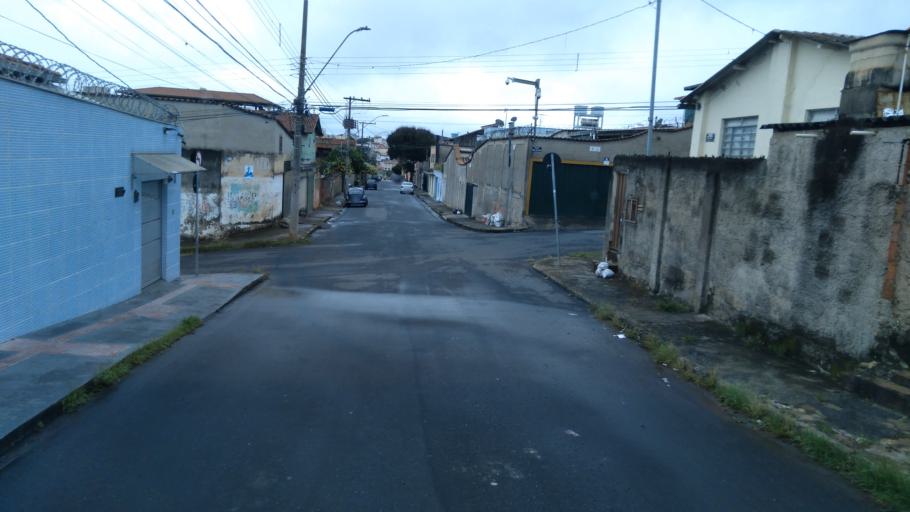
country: BR
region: Minas Gerais
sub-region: Belo Horizonte
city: Belo Horizonte
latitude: -19.9174
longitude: -43.9008
